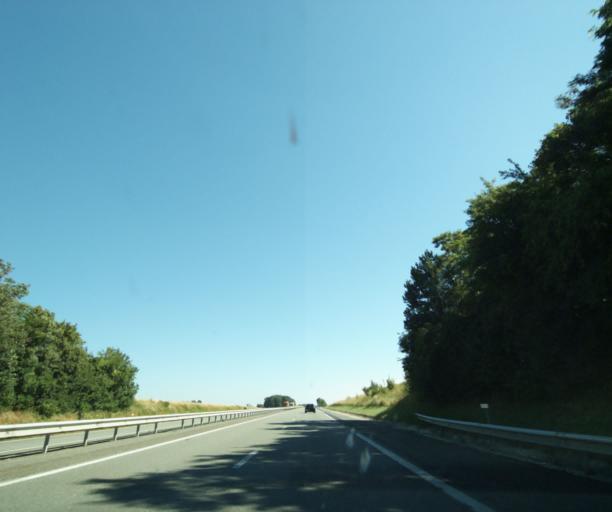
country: FR
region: Champagne-Ardenne
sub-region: Departement de la Haute-Marne
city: Avrecourt
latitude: 47.9997
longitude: 5.5152
